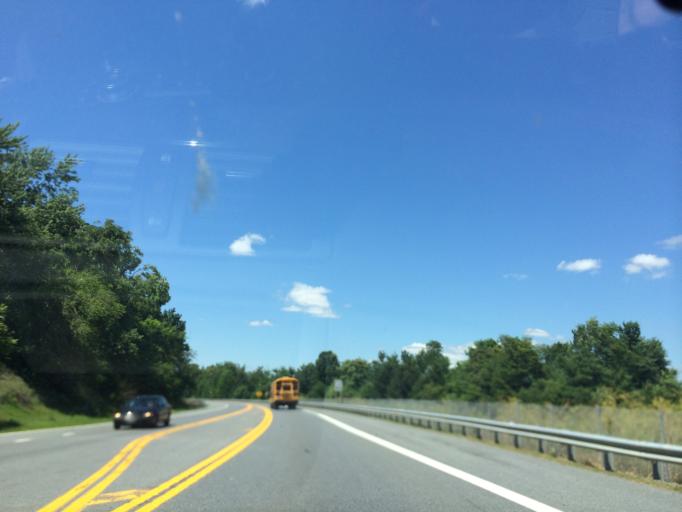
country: US
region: Maryland
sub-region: Frederick County
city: Woodsboro
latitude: 39.5331
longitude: -77.3113
